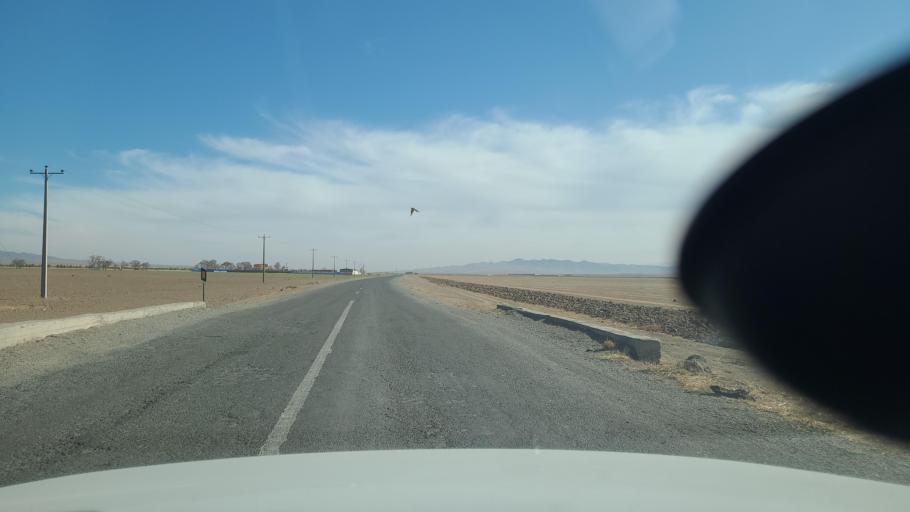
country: IR
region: Razavi Khorasan
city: Dowlatabad
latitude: 35.6000
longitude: 59.4644
